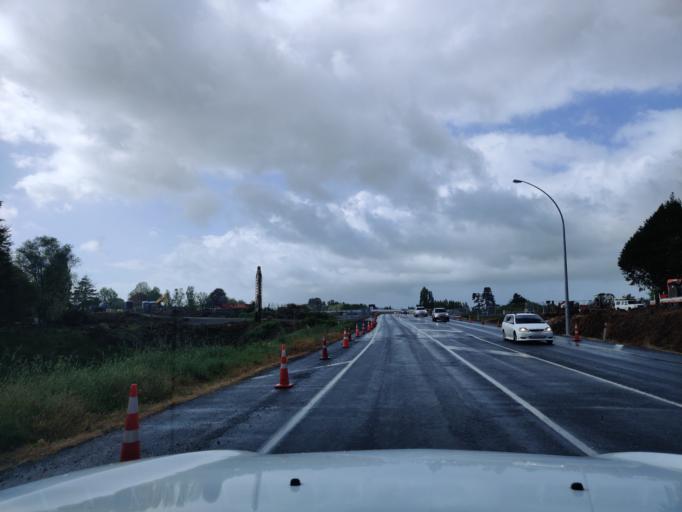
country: NZ
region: Waikato
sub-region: Hamilton City
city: Hamilton
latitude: -37.8131
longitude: 175.3407
